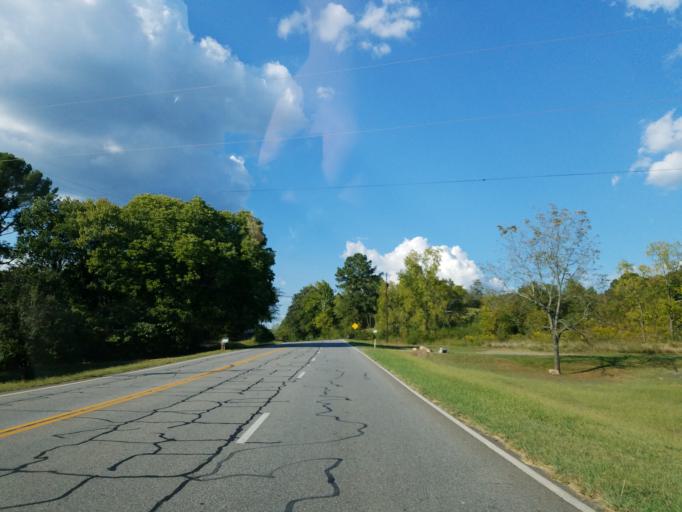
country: US
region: Georgia
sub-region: Bartow County
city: Rydal
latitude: 34.4863
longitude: -84.7064
